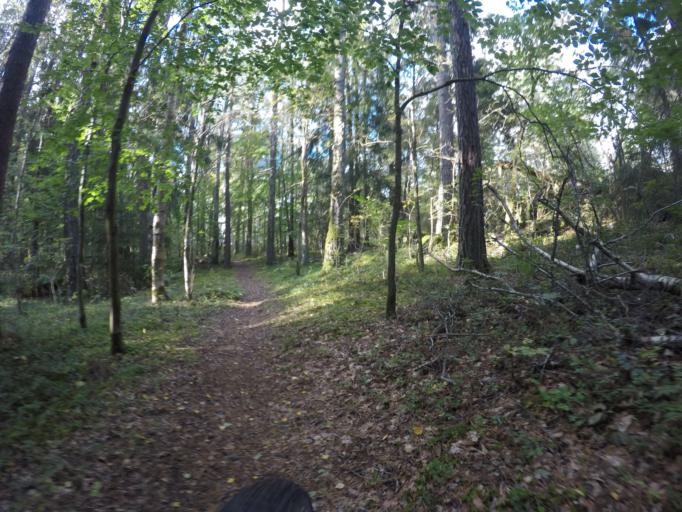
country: SE
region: Vaestmanland
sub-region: Kopings Kommun
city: Koping
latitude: 59.5116
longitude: 16.0101
